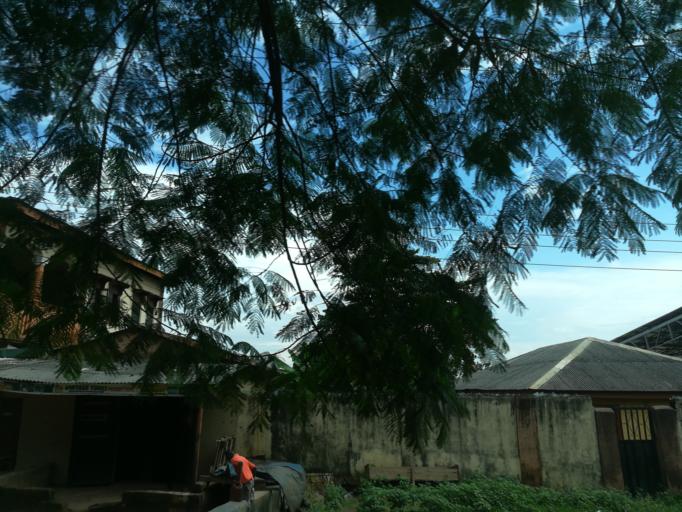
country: NG
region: Lagos
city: Ikorodu
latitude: 6.6128
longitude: 3.5028
